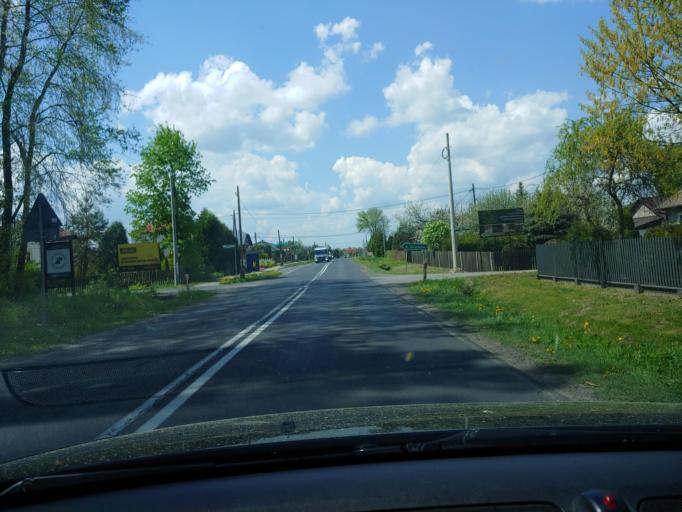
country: PL
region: Subcarpathian Voivodeship
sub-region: Powiat mielecki
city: Wadowice Gorne
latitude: 50.2593
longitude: 21.3421
